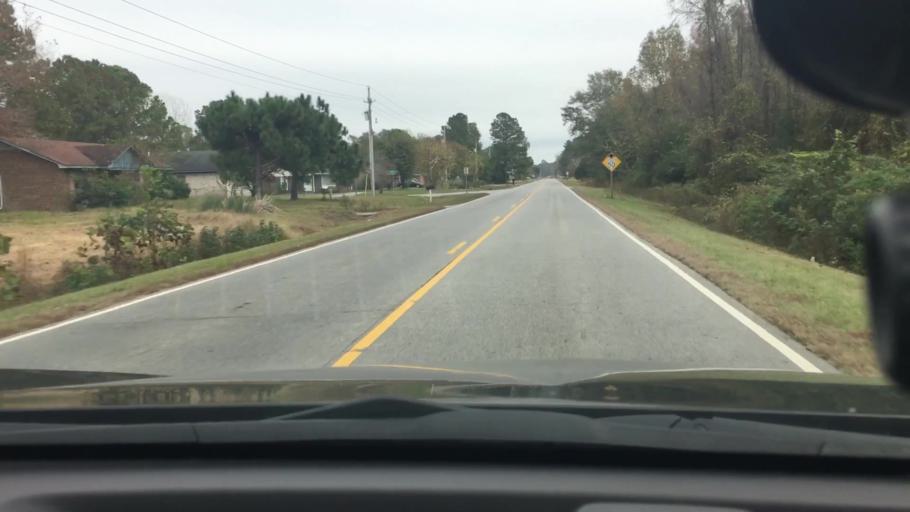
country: US
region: North Carolina
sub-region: Pitt County
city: Greenville
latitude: 35.6315
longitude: -77.3553
